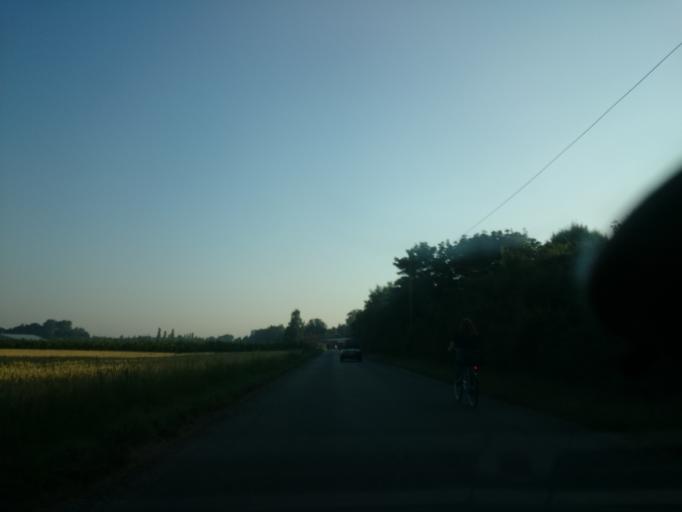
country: DE
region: Bavaria
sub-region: Swabia
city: Konigsbrunn
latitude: 48.3036
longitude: 10.8932
